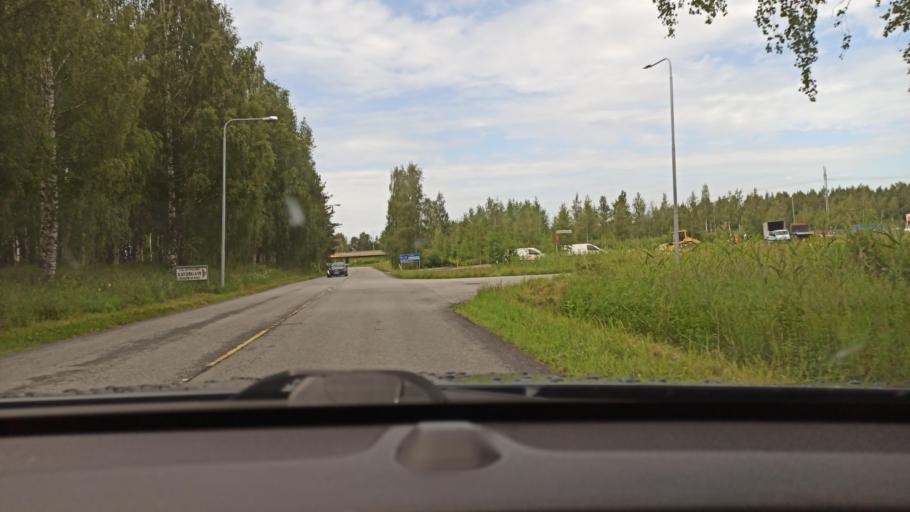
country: FI
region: Satakunta
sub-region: Pori
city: Pori
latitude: 61.5109
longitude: 21.7735
